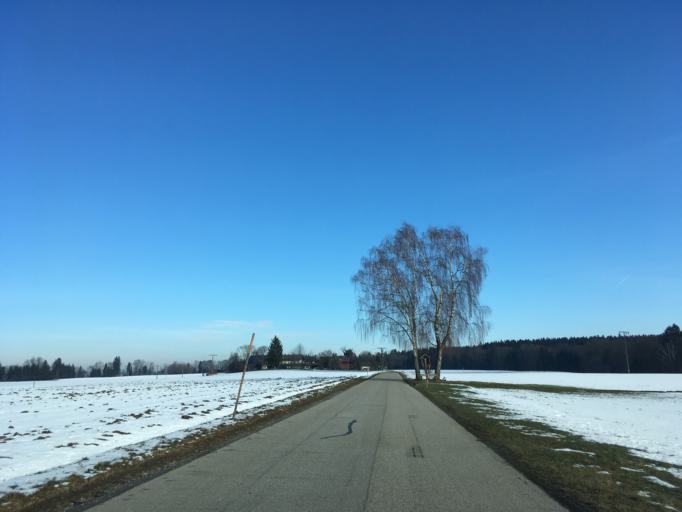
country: DE
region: Bavaria
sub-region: Upper Bavaria
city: Schechen
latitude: 47.9092
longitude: 12.1488
